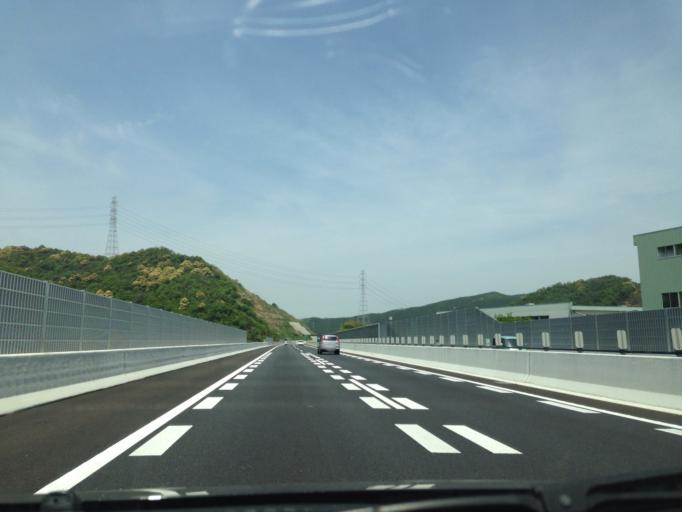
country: JP
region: Aichi
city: Gamagori
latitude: 34.9245
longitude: 137.2708
